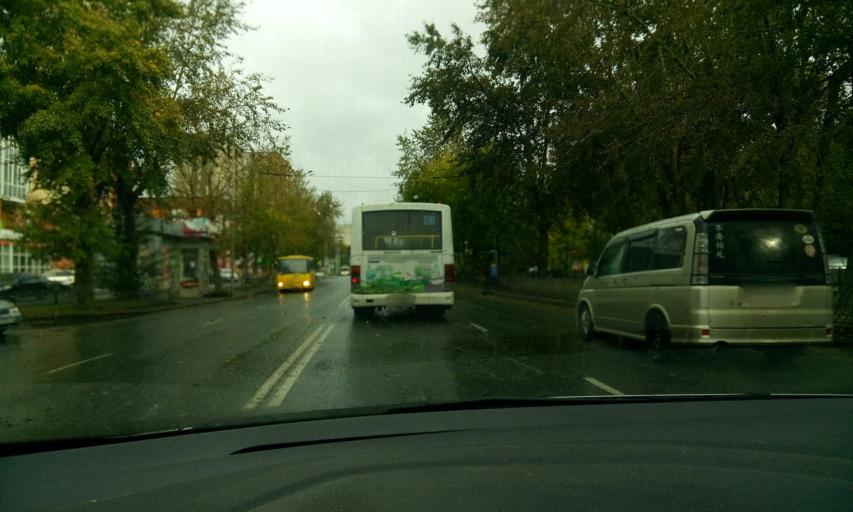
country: RU
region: Sverdlovsk
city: Yekaterinburg
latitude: 56.8081
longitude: 60.6238
